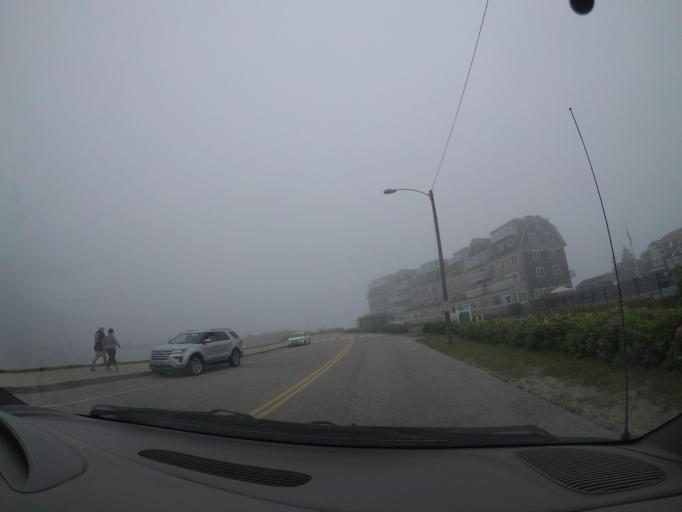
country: US
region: Maine
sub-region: York County
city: Kennebunkport
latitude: 43.3459
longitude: -70.4865
